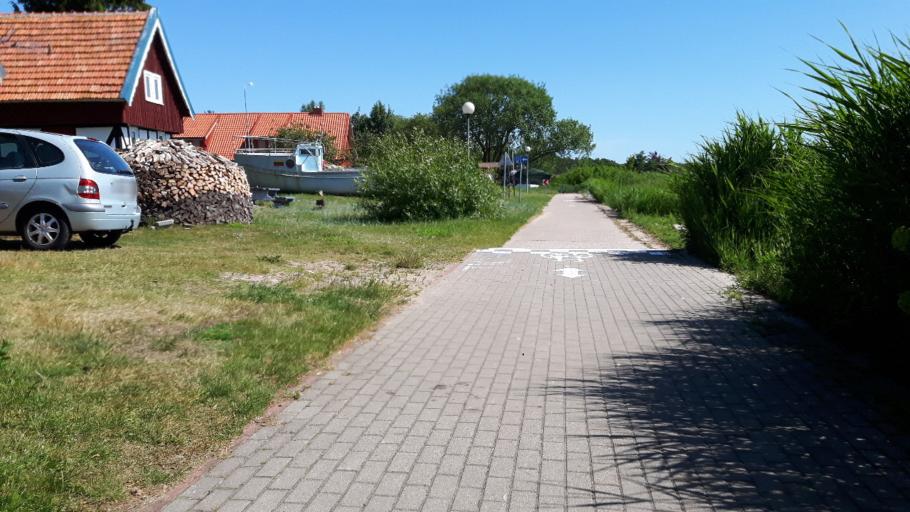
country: LT
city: Nida
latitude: 55.3173
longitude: 21.0206
